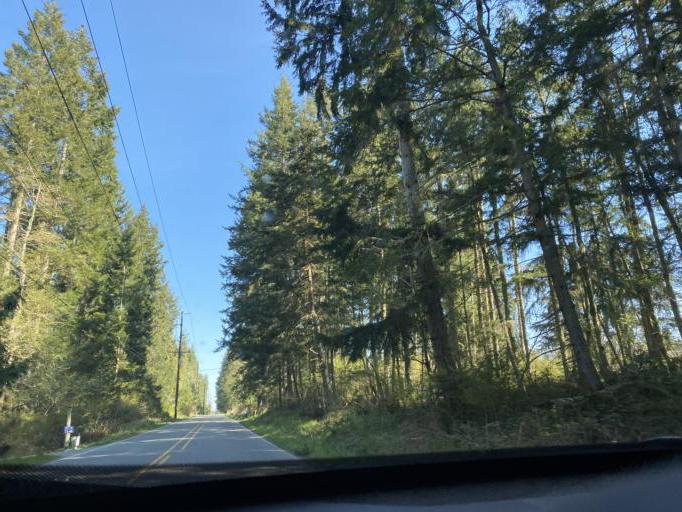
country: US
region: Washington
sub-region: Island County
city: Freeland
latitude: 48.0817
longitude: -122.5830
